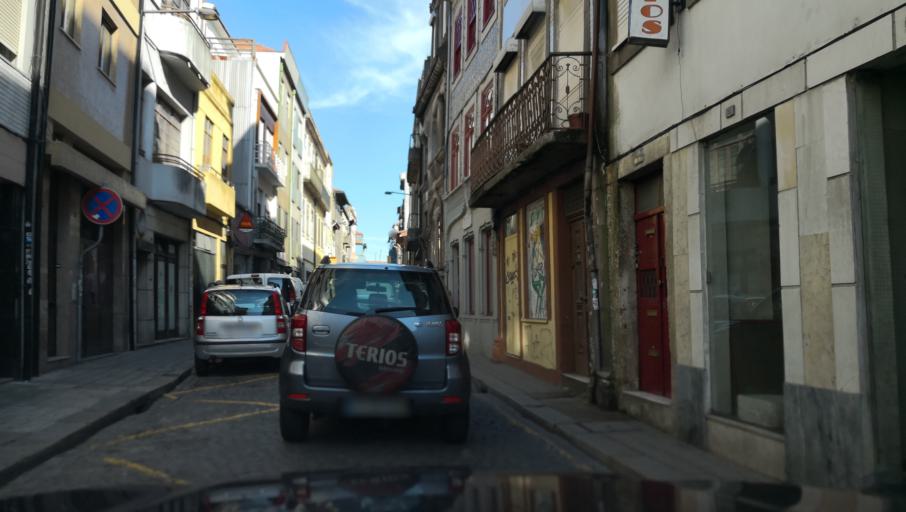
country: PT
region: Porto
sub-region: Porto
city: Porto
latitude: 41.1518
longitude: -8.6138
